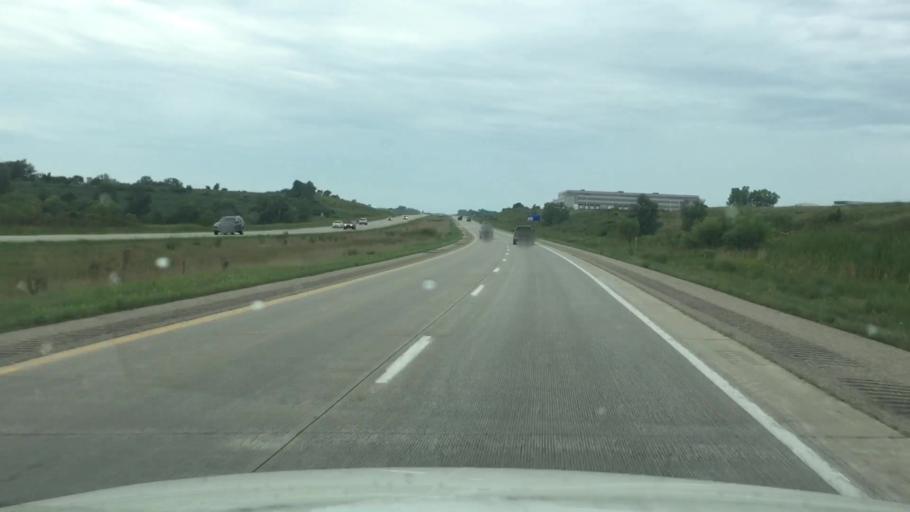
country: US
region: Iowa
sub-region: Warren County
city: Norwalk
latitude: 41.5145
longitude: -93.6638
